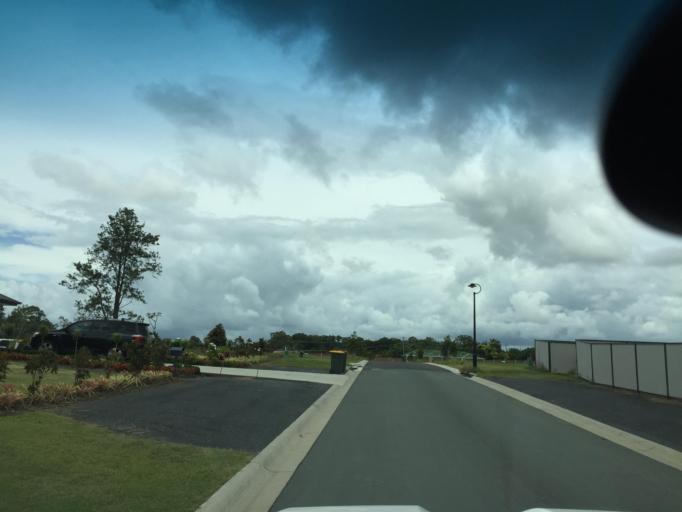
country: AU
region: Queensland
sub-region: Moreton Bay
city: Caboolture
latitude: -27.0428
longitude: 152.9280
